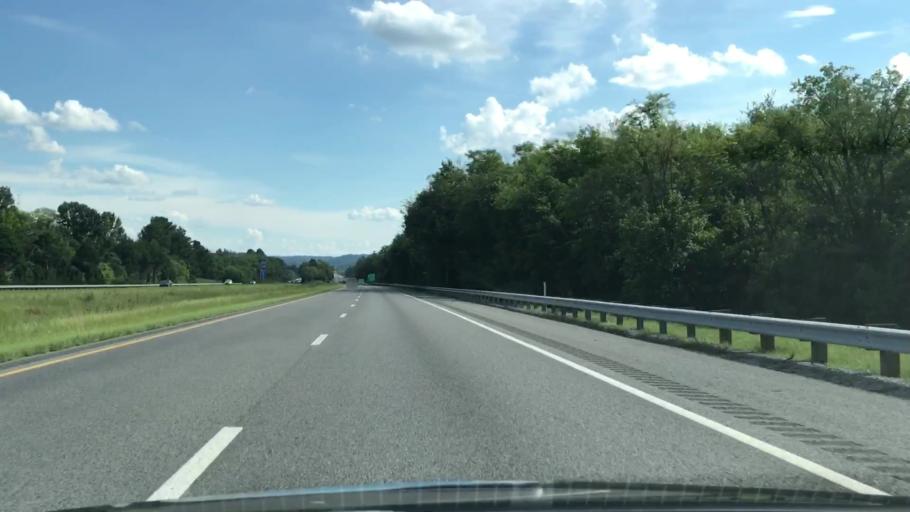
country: US
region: Tennessee
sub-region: Marshall County
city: Lewisburg
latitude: 35.4600
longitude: -86.8865
